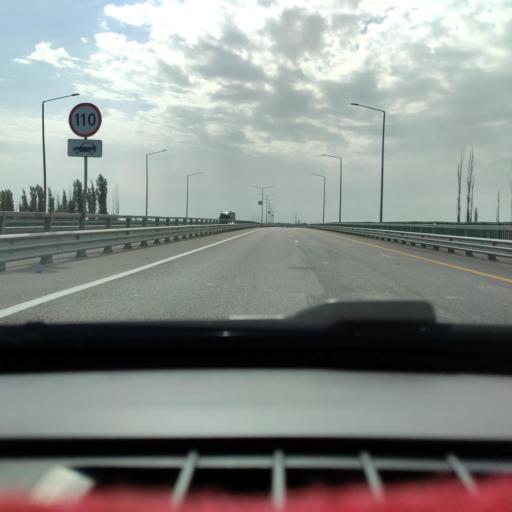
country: RU
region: Voronezj
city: Kashirskoye
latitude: 51.4827
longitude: 39.5428
